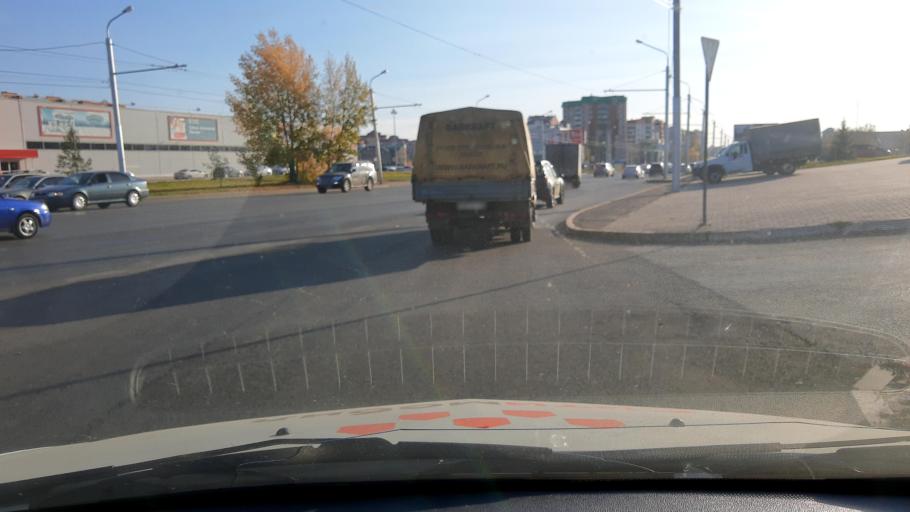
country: RU
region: Bashkortostan
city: Ufa
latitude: 54.7830
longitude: 56.0728
